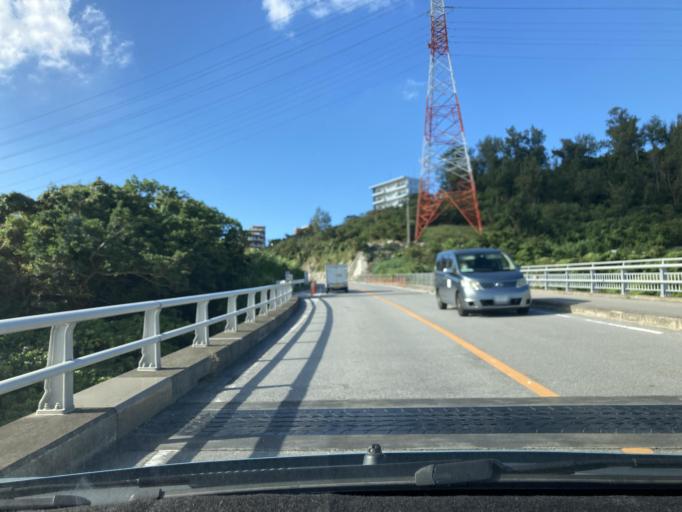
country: JP
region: Okinawa
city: Okinawa
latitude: 26.3393
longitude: 127.8337
